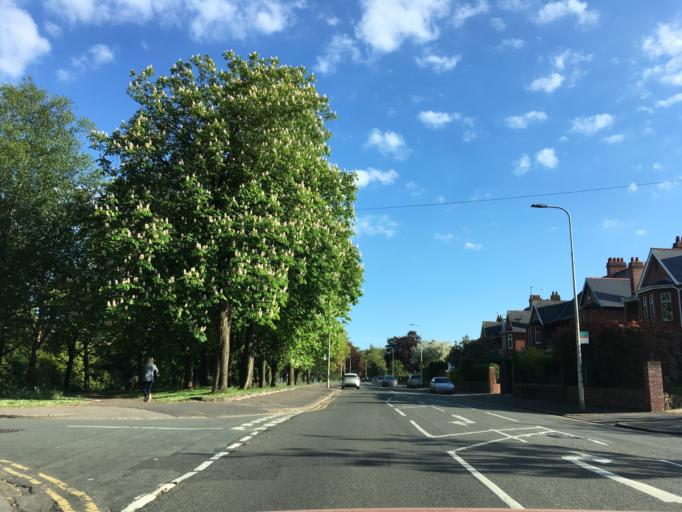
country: GB
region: Wales
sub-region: Cardiff
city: Cardiff
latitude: 51.5141
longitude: -3.1770
